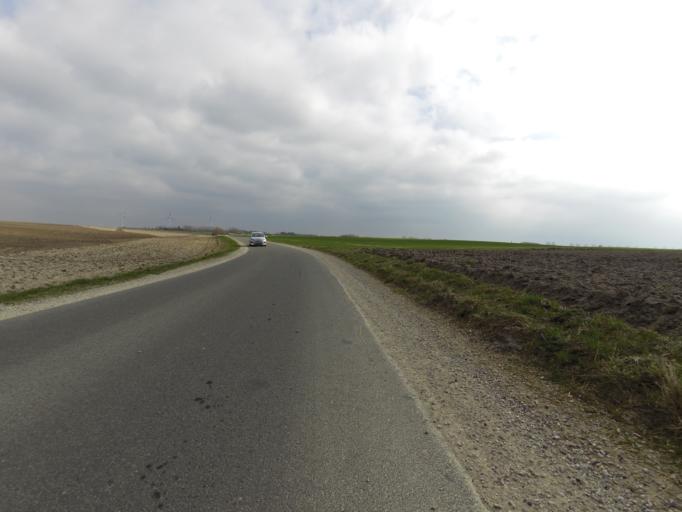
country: DK
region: Central Jutland
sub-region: Holstebro Kommune
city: Holstebro
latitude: 56.4351
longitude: 8.6720
